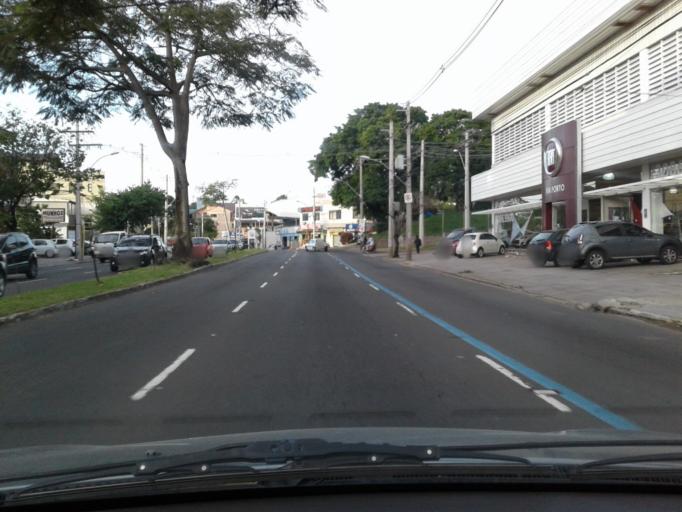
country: BR
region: Rio Grande do Sul
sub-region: Porto Alegre
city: Porto Alegre
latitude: -30.0916
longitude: -51.2210
